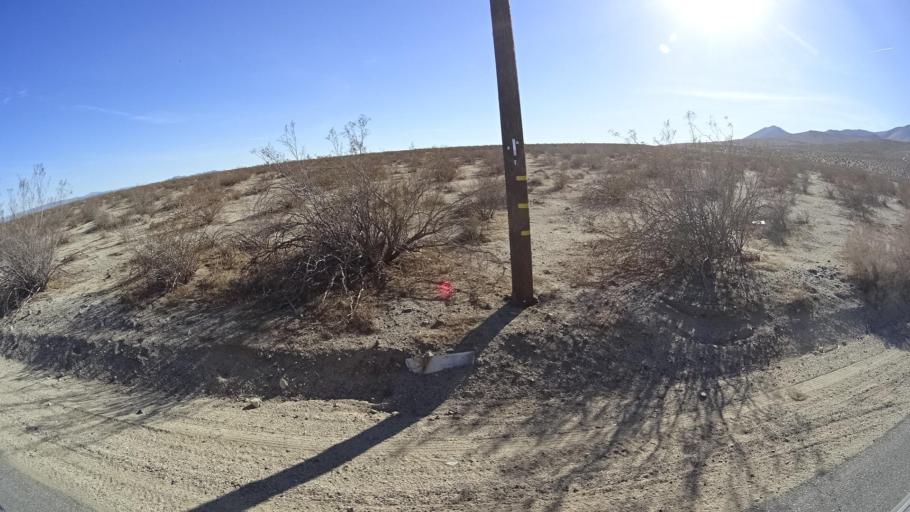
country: US
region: California
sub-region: Kern County
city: Inyokern
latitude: 35.6811
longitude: -117.8650
